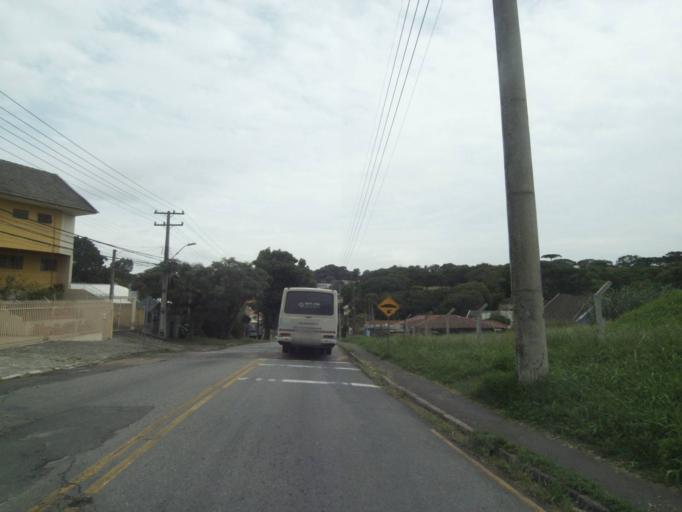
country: BR
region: Parana
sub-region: Curitiba
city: Curitiba
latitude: -25.4121
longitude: -49.3030
